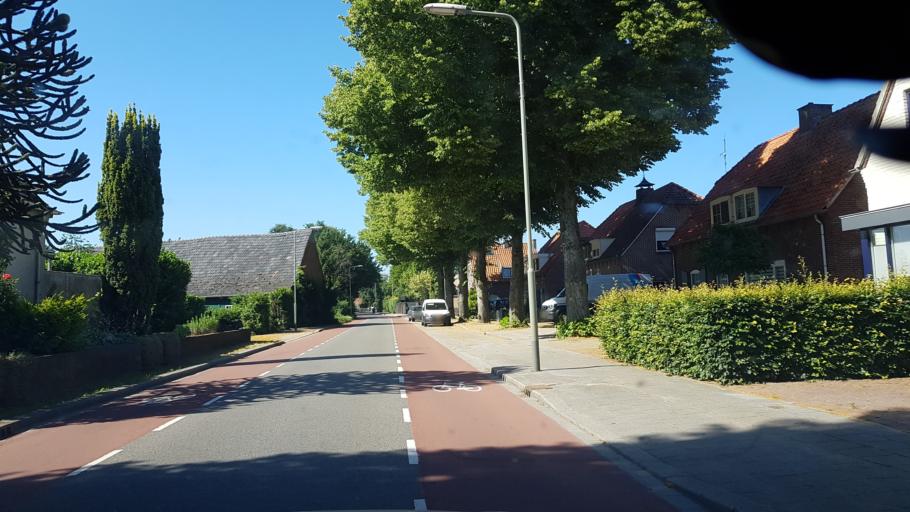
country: NL
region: Limburg
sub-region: Gemeente Gennep
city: Gennep
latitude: 51.7248
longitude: 5.9526
